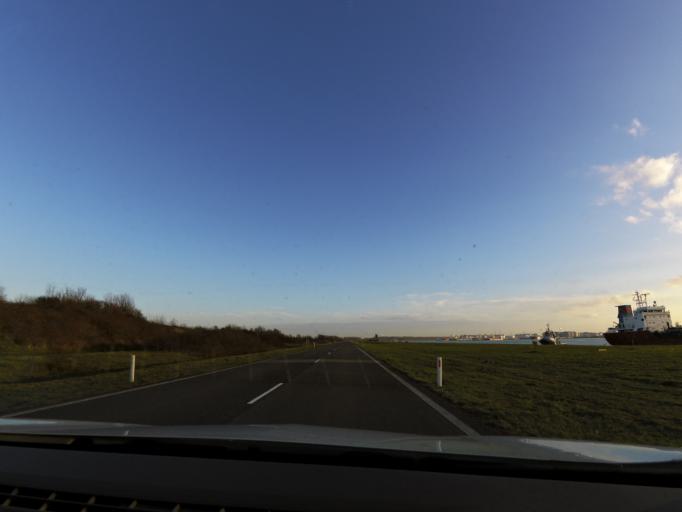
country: NL
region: South Holland
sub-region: Gemeente Westland
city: Maasdijk
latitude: 51.9343
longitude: 4.1974
